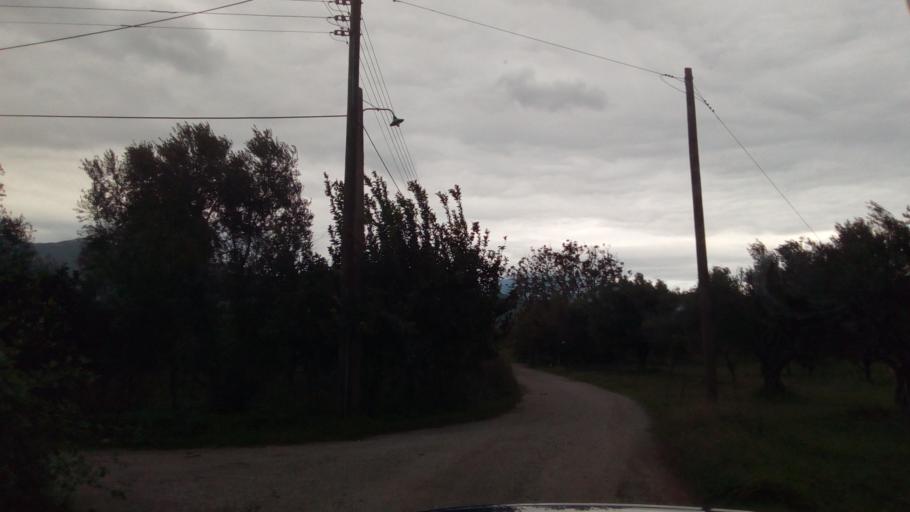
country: GR
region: West Greece
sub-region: Nomos Aitolias kai Akarnanias
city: Nafpaktos
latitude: 38.3907
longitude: 21.8869
